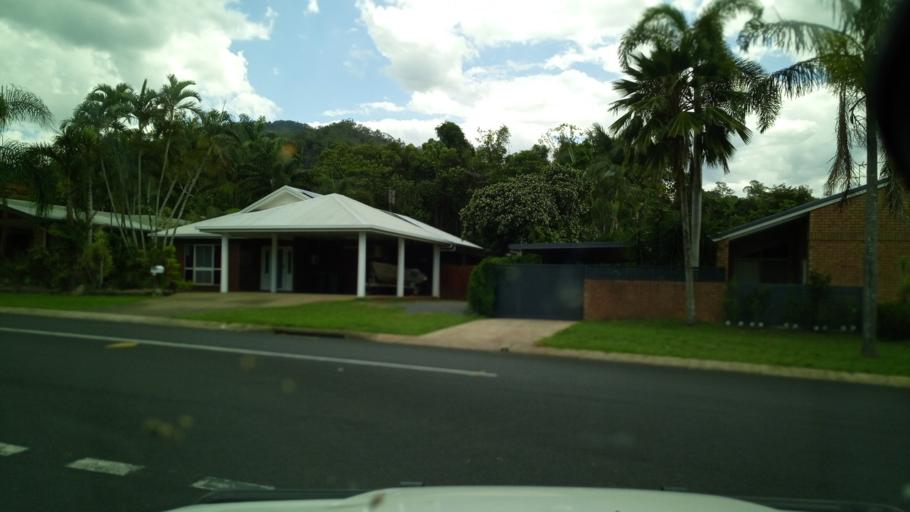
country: AU
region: Queensland
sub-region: Cairns
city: Redlynch
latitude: -16.9051
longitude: 145.7136
